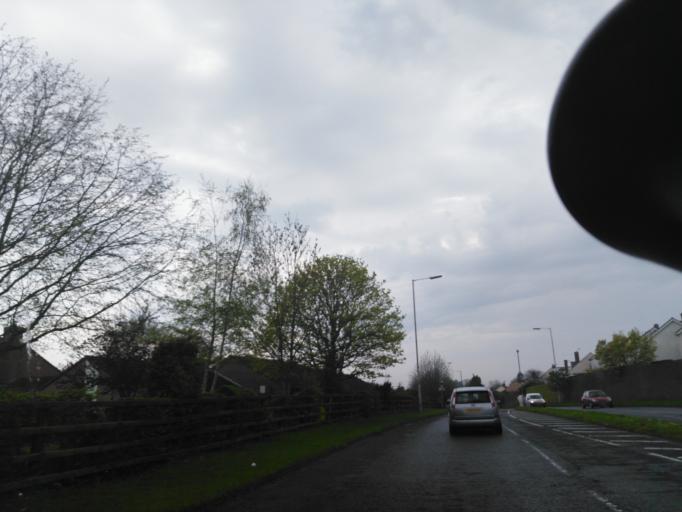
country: GB
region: England
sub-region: Somerset
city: Street
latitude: 51.1297
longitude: -2.7435
